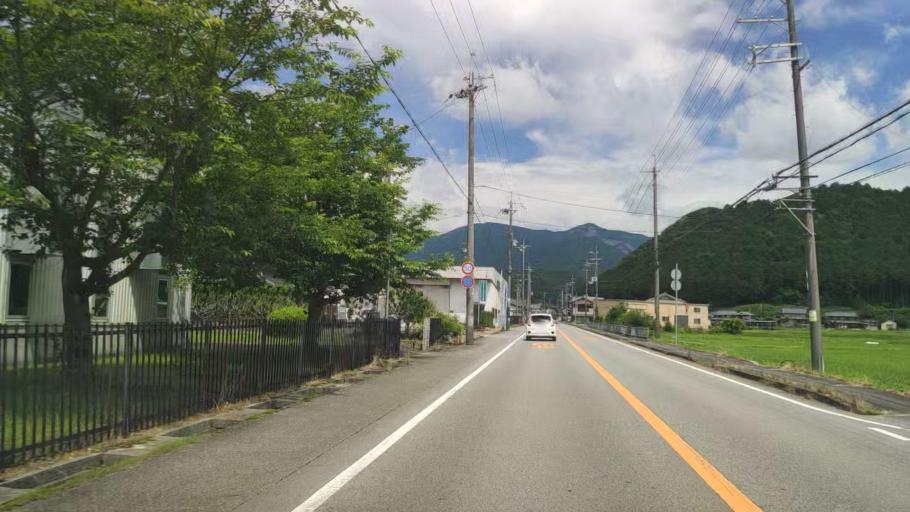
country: JP
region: Hyogo
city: Nishiwaki
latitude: 35.0755
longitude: 134.8976
